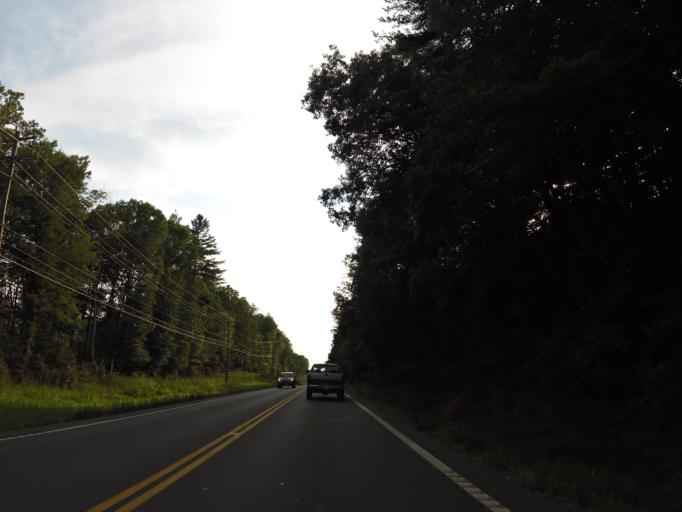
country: US
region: Tennessee
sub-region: Roane County
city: Oliver Springs
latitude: 36.0428
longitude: -84.3709
